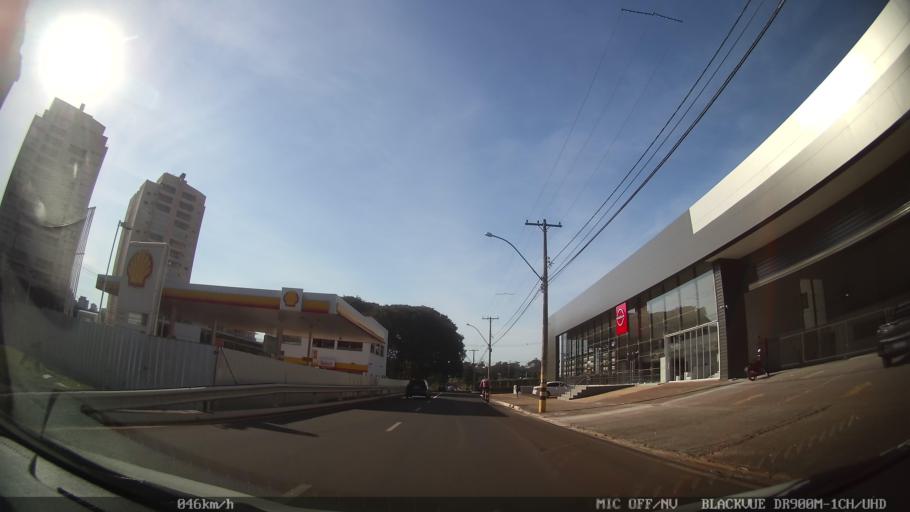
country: BR
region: Sao Paulo
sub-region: Ribeirao Preto
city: Ribeirao Preto
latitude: -21.2167
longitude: -47.8198
